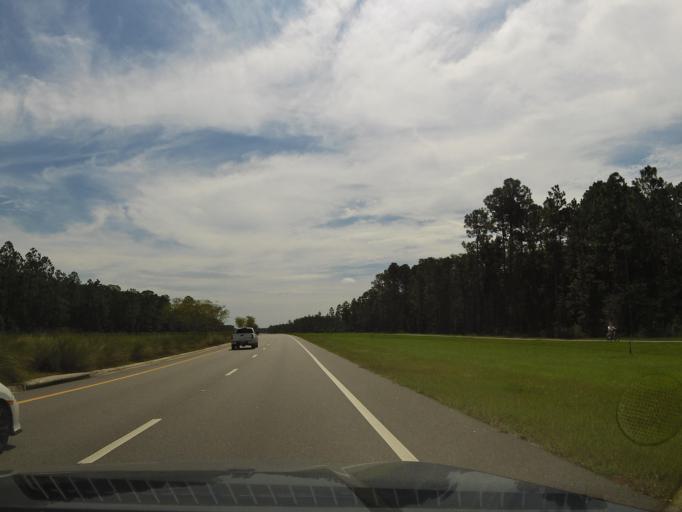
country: US
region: Florida
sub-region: Saint Johns County
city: Fruit Cove
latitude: 30.0240
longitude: -81.5209
